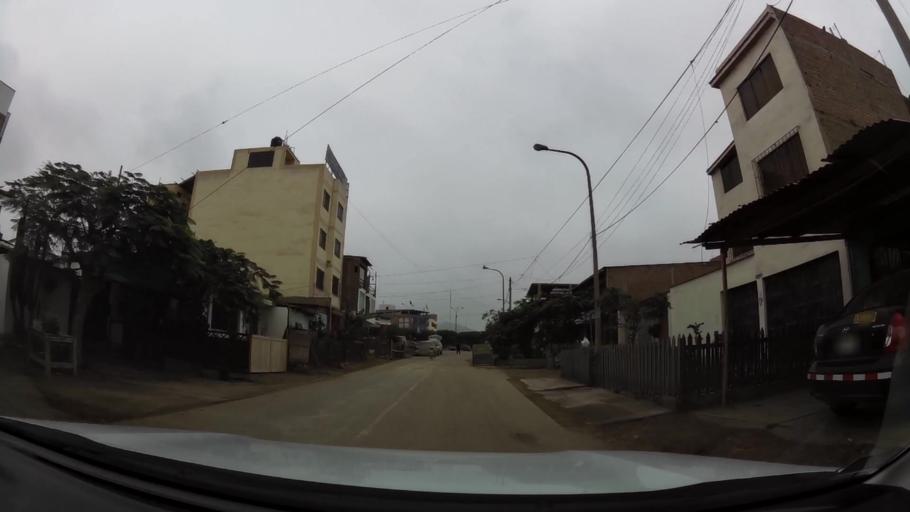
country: PE
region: Lima
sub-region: Lima
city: Punta Hermosa
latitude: -12.2373
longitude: -76.9098
